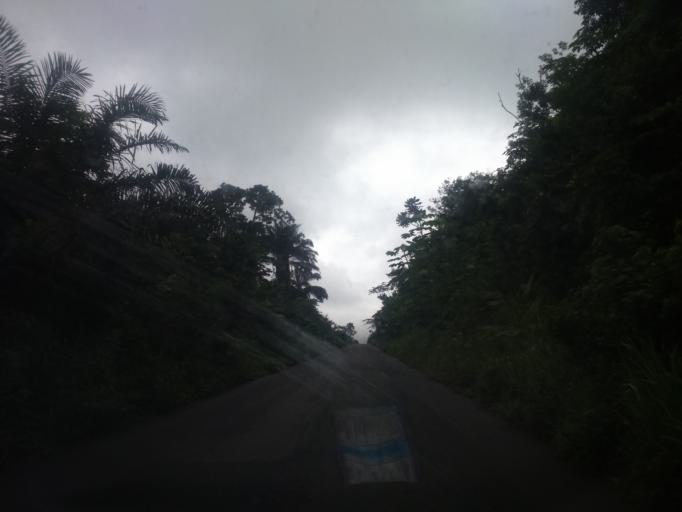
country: CI
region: Sud-Comoe
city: Bonoua
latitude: 5.2789
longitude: -3.4948
